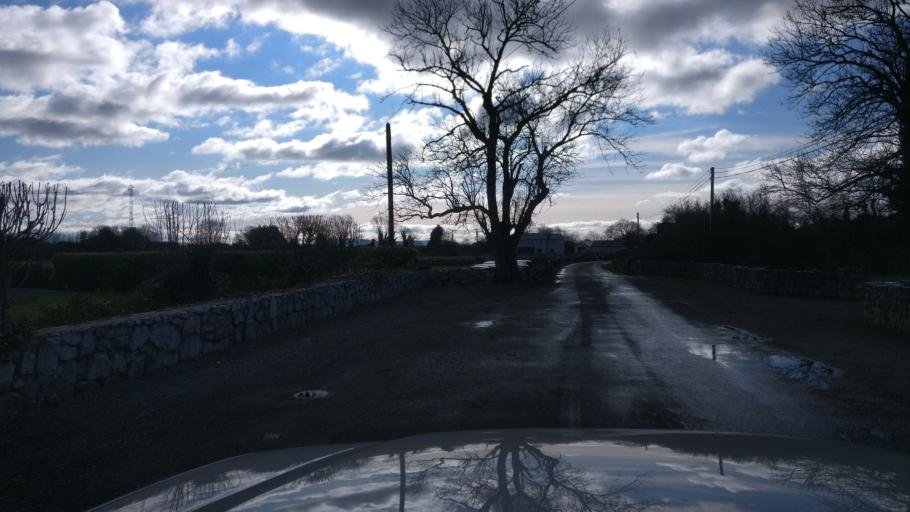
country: IE
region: Connaught
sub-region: County Galway
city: Oranmore
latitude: 53.2837
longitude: -8.8935
